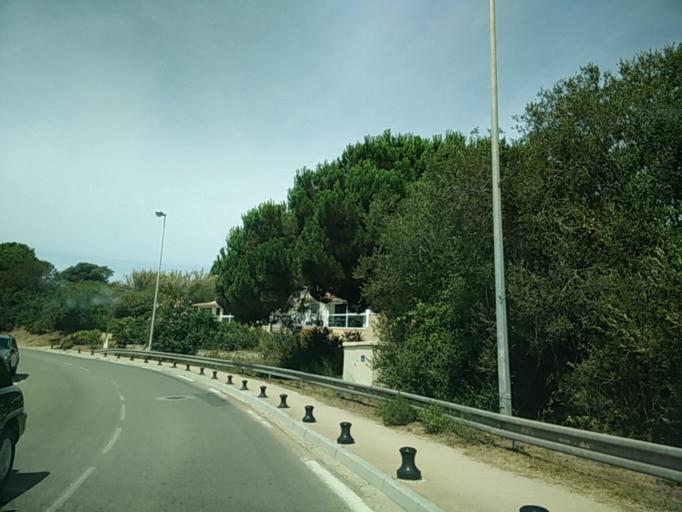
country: FR
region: Corsica
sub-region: Departement de la Corse-du-Sud
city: Pietrosella
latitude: 41.8343
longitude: 8.7827
